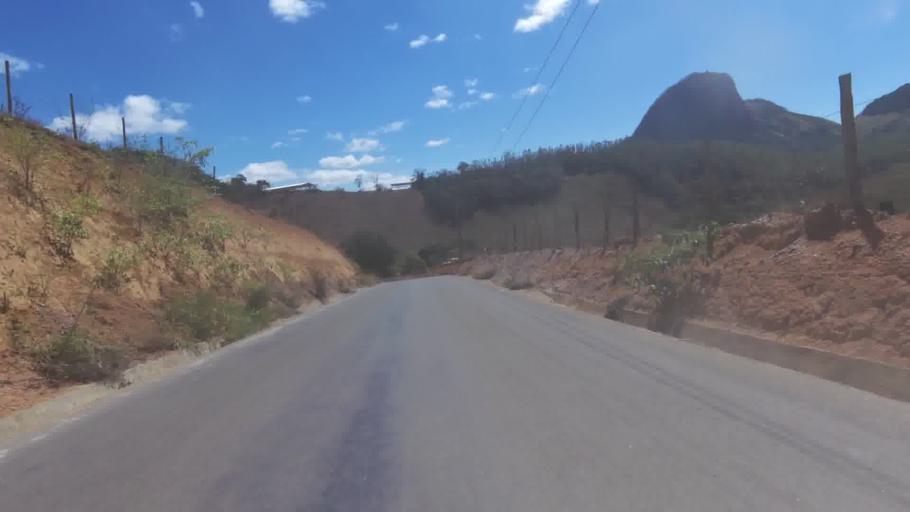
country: BR
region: Espirito Santo
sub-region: Cachoeiro De Itapemirim
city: Cachoeiro de Itapemirim
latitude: -20.9210
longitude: -41.2032
